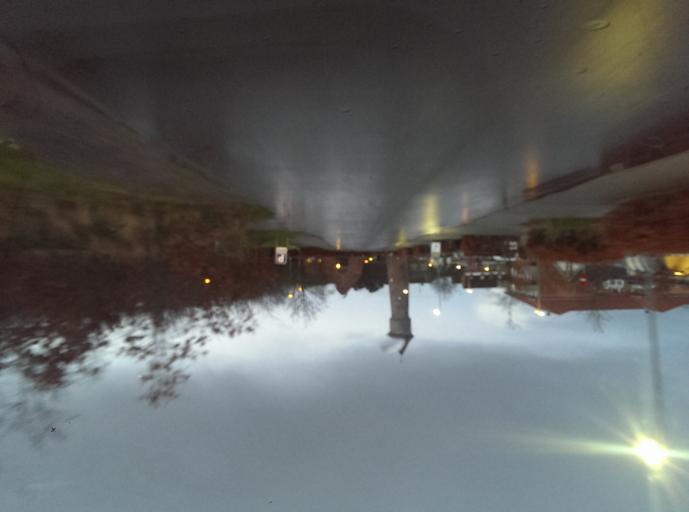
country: DK
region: South Denmark
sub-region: Esbjerg Kommune
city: Bramming
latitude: 55.4647
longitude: 8.6975
